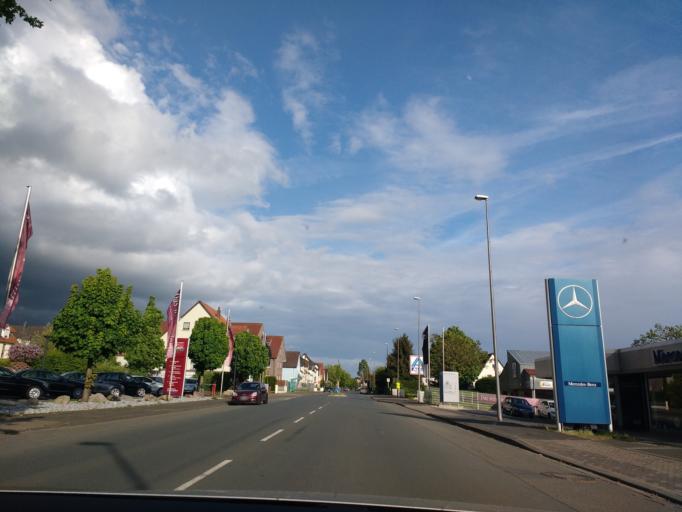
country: DE
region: North Rhine-Westphalia
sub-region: Regierungsbezirk Detmold
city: Bad Salzuflen
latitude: 52.0892
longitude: 8.7306
